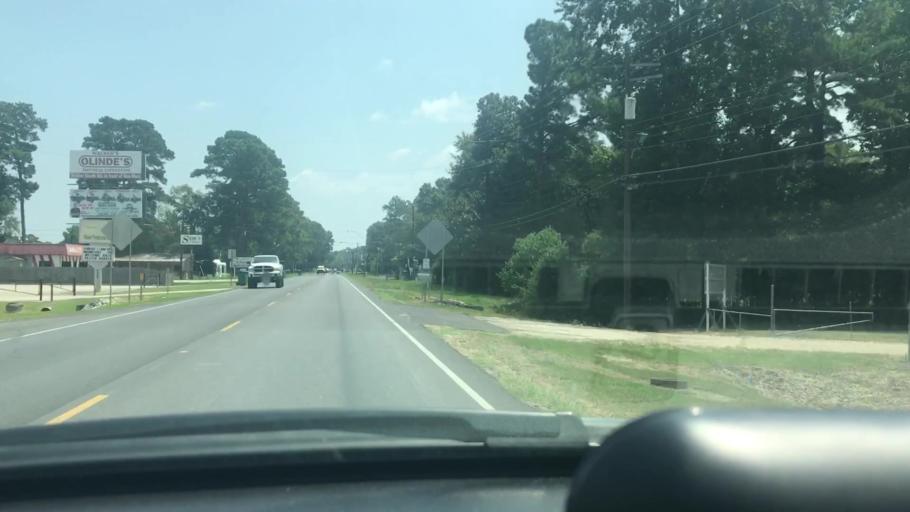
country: US
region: Louisiana
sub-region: Livingston Parish
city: Walker
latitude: 30.4873
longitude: -90.8695
